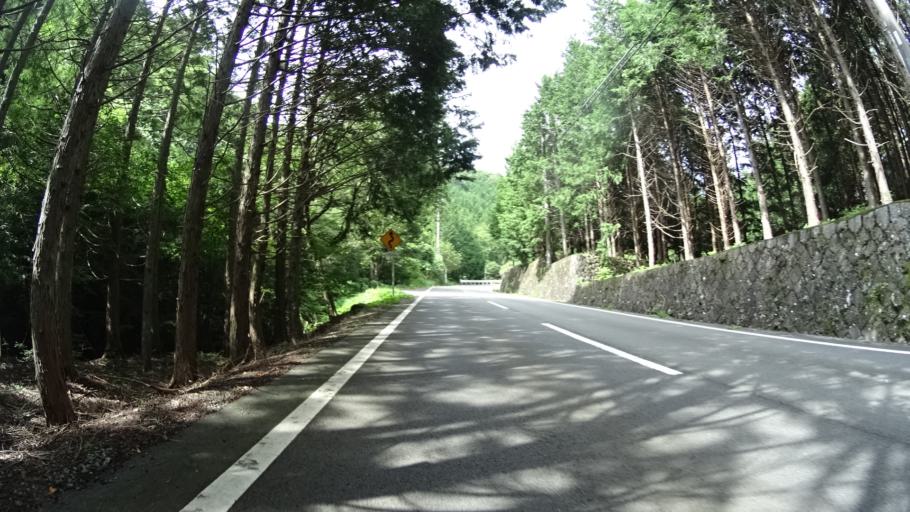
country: JP
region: Yamanashi
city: Kofu-shi
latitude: 35.7627
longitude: 138.5451
